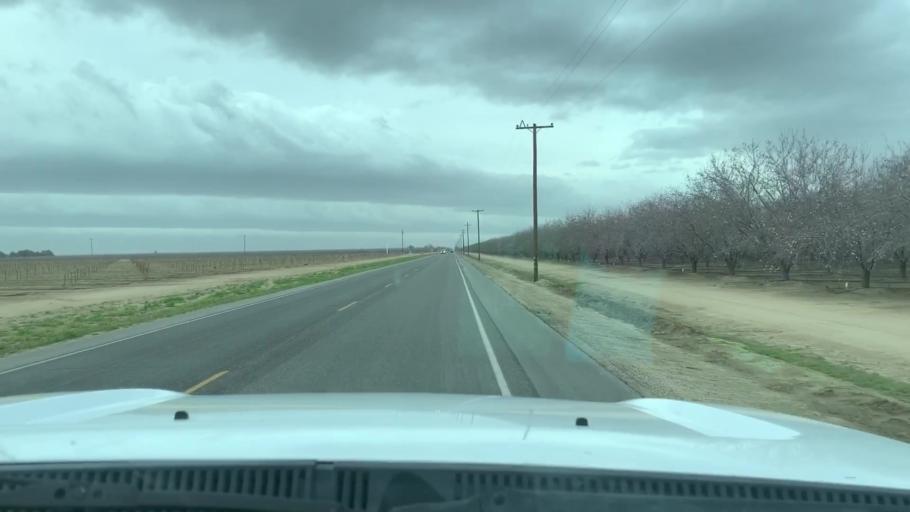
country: US
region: California
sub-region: Kern County
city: Wasco
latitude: 35.5581
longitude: -119.3004
